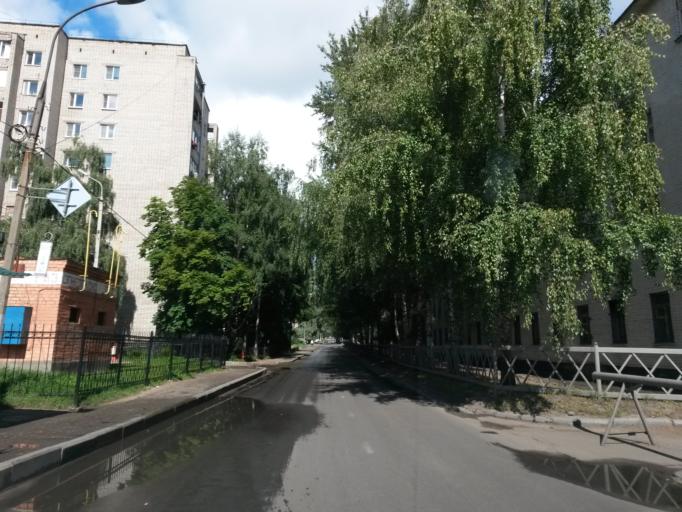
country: RU
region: Jaroslavl
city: Yaroslavl
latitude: 57.6186
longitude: 39.8627
